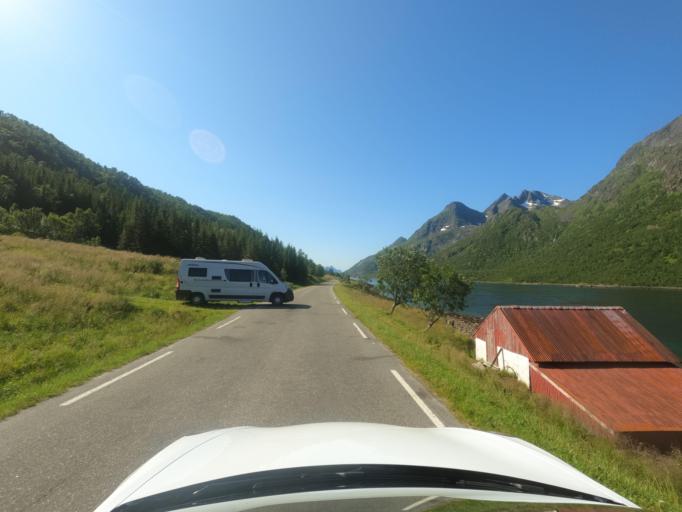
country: NO
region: Nordland
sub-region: Hadsel
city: Stokmarknes
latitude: 68.4106
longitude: 15.1286
